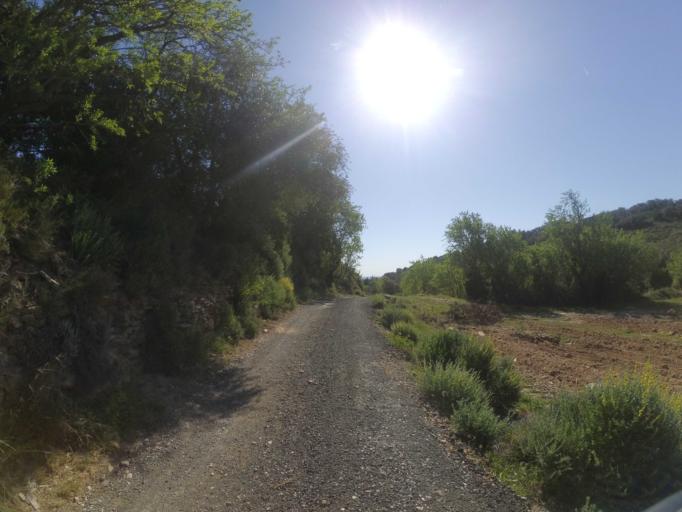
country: FR
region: Languedoc-Roussillon
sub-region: Departement des Pyrenees-Orientales
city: Baixas
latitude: 42.7609
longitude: 2.7834
